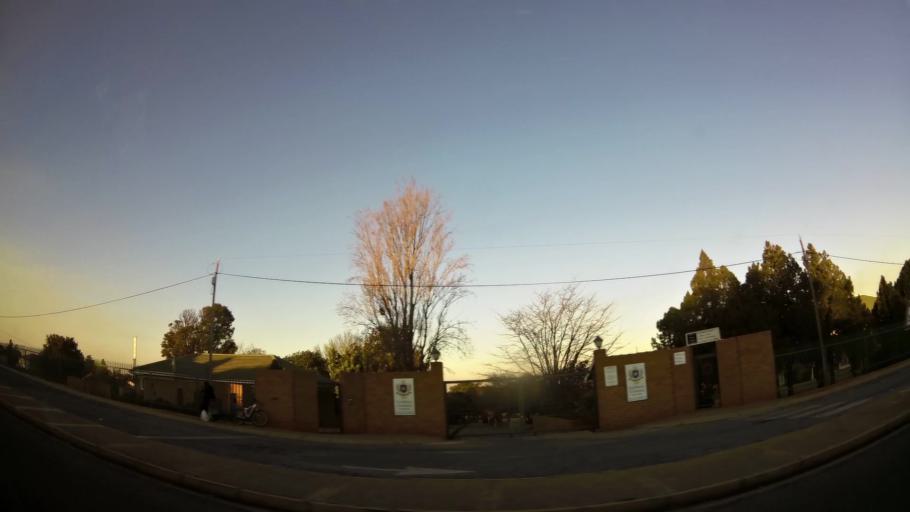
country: ZA
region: Gauteng
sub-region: City of Johannesburg Metropolitan Municipality
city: Roodepoort
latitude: -26.1487
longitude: 27.8941
